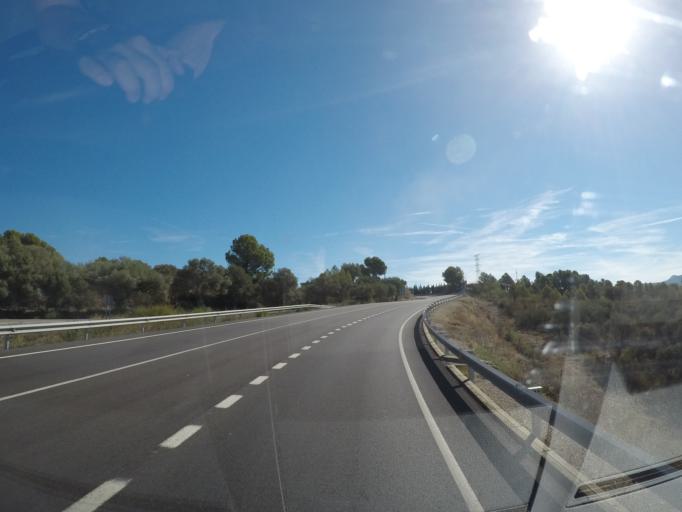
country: ES
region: Catalonia
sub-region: Provincia de Tarragona
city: Garcia
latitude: 41.1061
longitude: 0.6704
